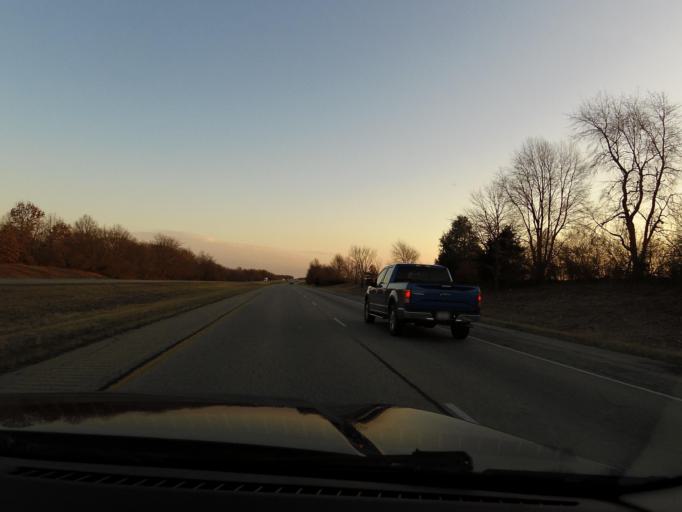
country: US
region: Illinois
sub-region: Marion County
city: Salem
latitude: 38.6949
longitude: -88.9627
